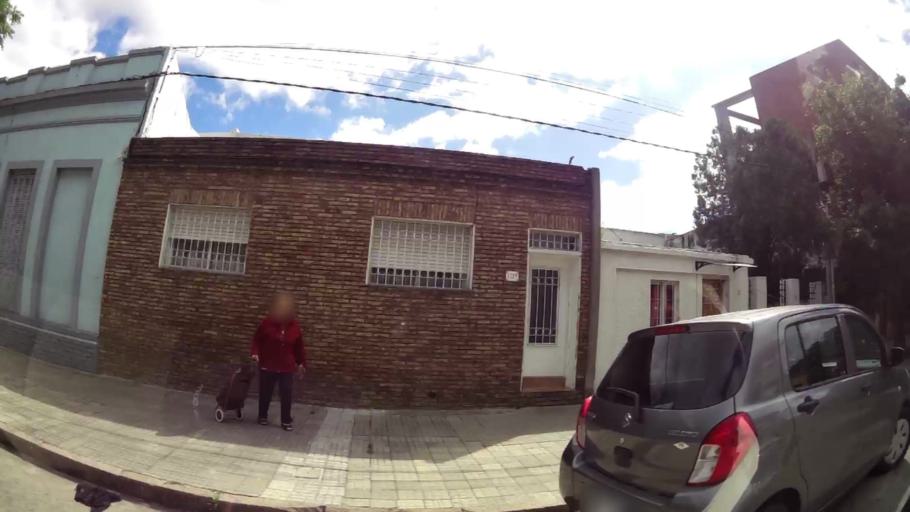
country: UY
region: Montevideo
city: Montevideo
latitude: -34.8750
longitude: -56.1804
